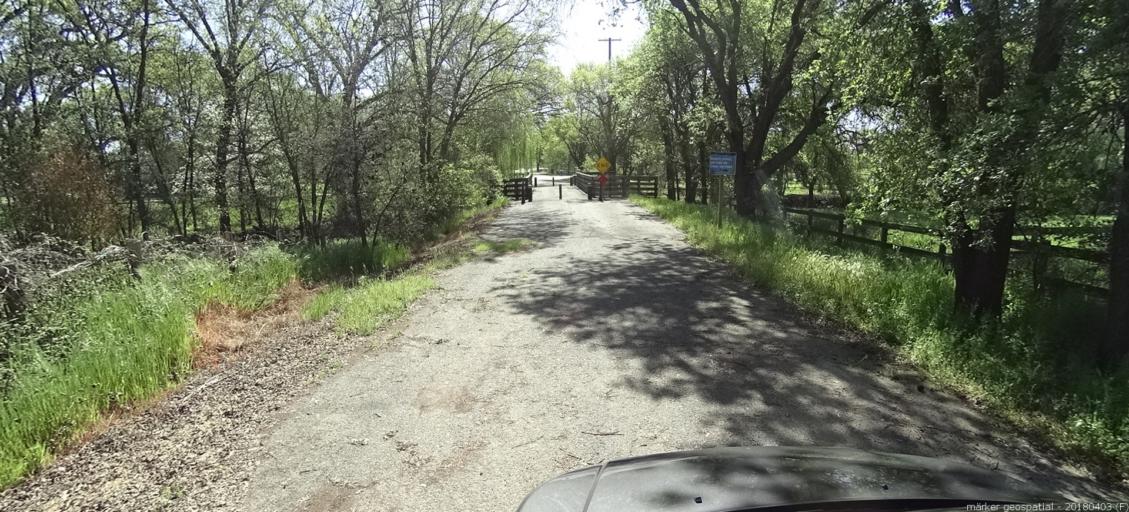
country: US
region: California
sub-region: Sacramento County
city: Wilton
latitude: 38.4246
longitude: -121.2019
